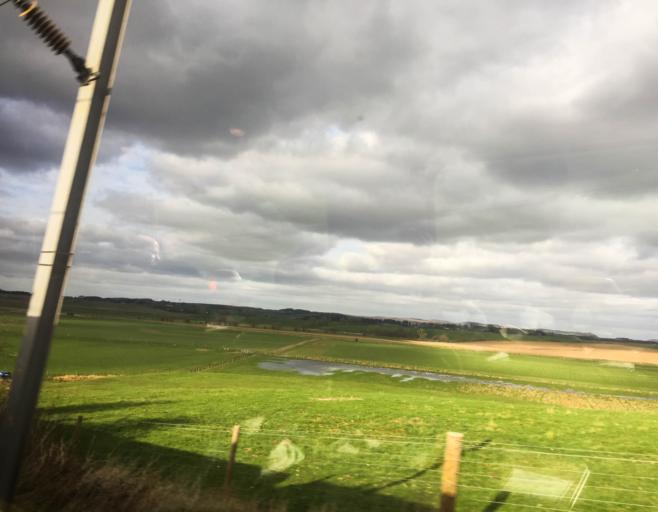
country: GB
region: Scotland
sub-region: South Lanarkshire
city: Carnwath
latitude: 55.6652
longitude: -3.6339
